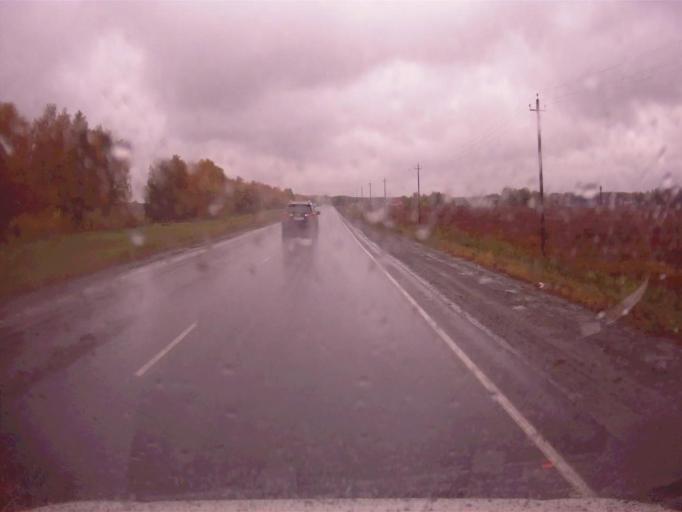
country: RU
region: Chelyabinsk
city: Argayash
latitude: 55.4041
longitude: 61.0642
